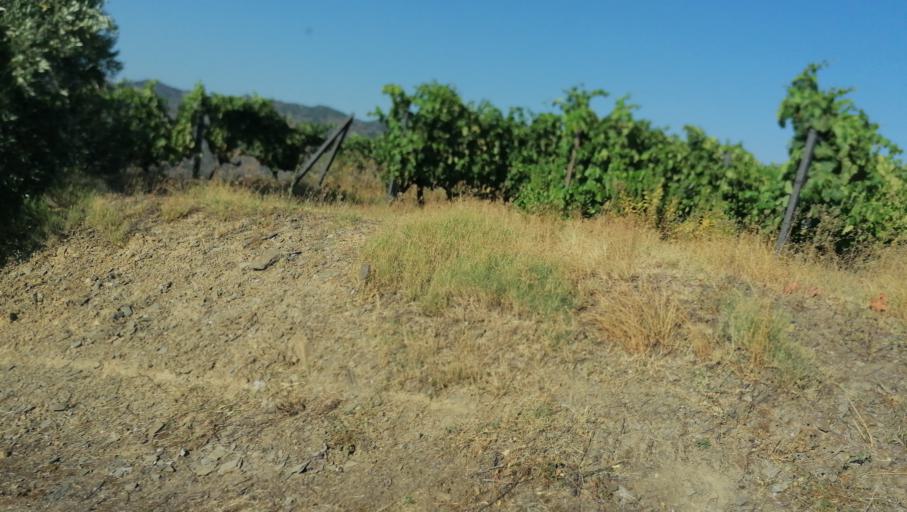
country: PT
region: Viseu
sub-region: Sao Joao da Pesqueira
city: Sao Joao da Pesqueira
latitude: 41.1806
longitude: -7.4035
